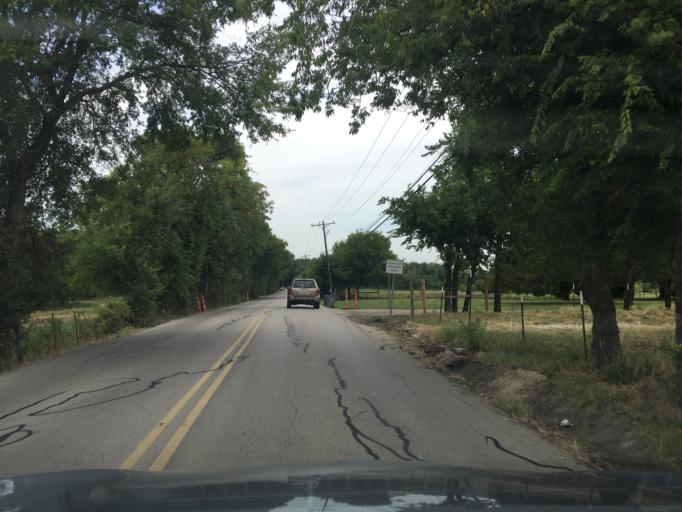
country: US
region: Texas
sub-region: Collin County
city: Saint Paul
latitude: 33.0313
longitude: -96.5772
